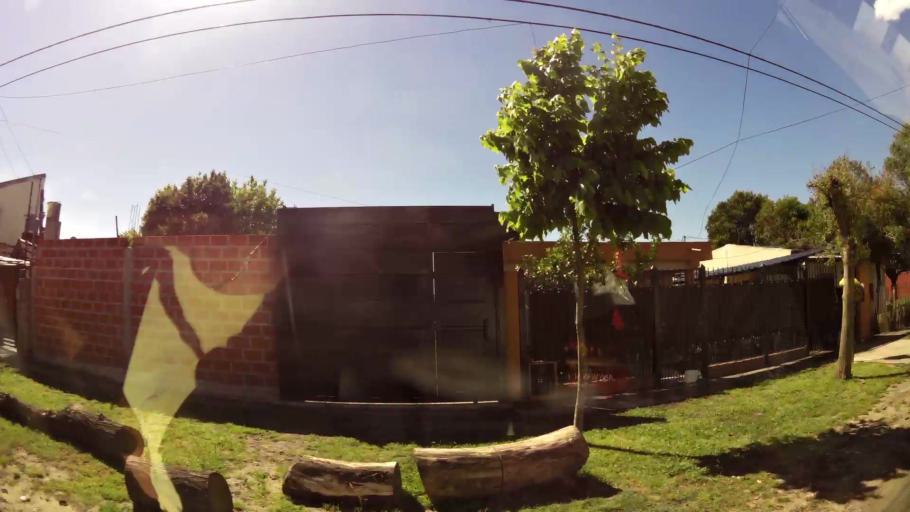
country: AR
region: Buenos Aires
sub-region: Partido de Almirante Brown
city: Adrogue
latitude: -34.7832
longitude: -58.3473
